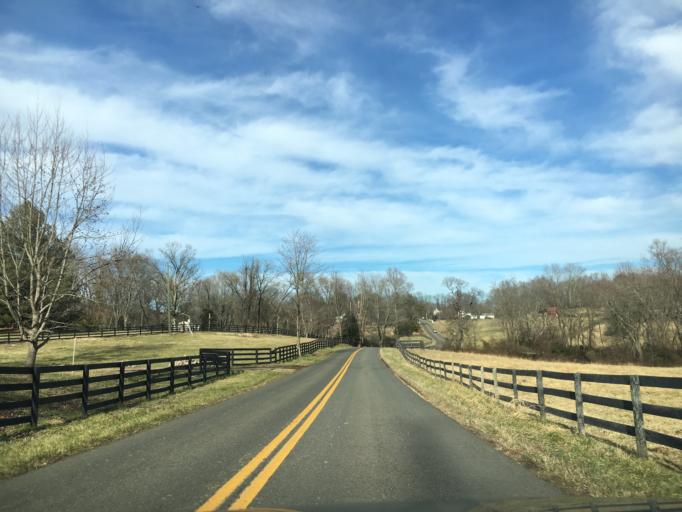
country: US
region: Virginia
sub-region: Warren County
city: Apple Mountain Lake
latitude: 38.8230
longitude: -77.9997
